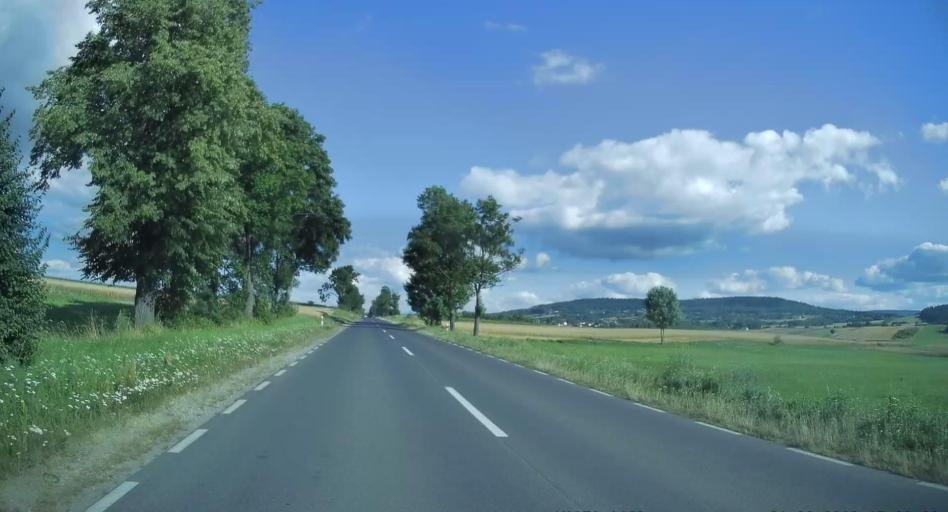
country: PL
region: Swietokrzyskie
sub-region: Powiat kielecki
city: Bodzentyn
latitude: 50.9533
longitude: 20.9213
